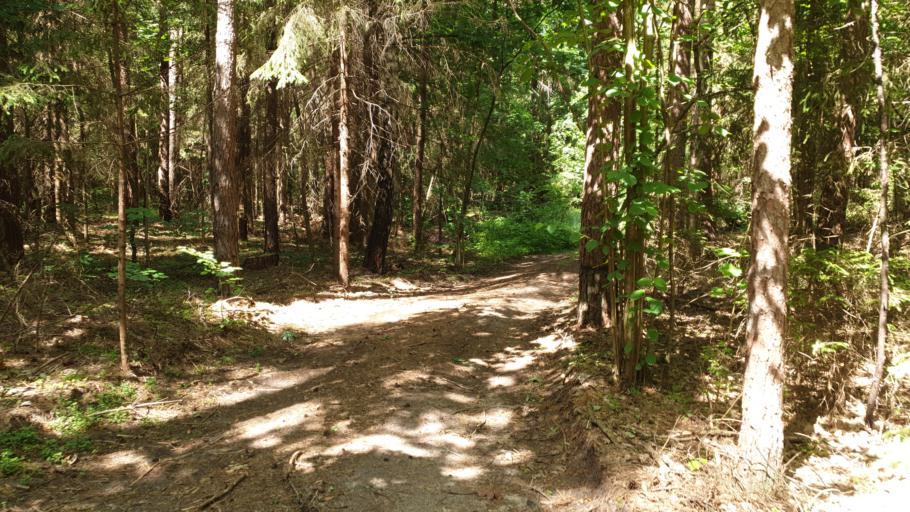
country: LT
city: Grigiskes
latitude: 54.7785
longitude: 24.9929
